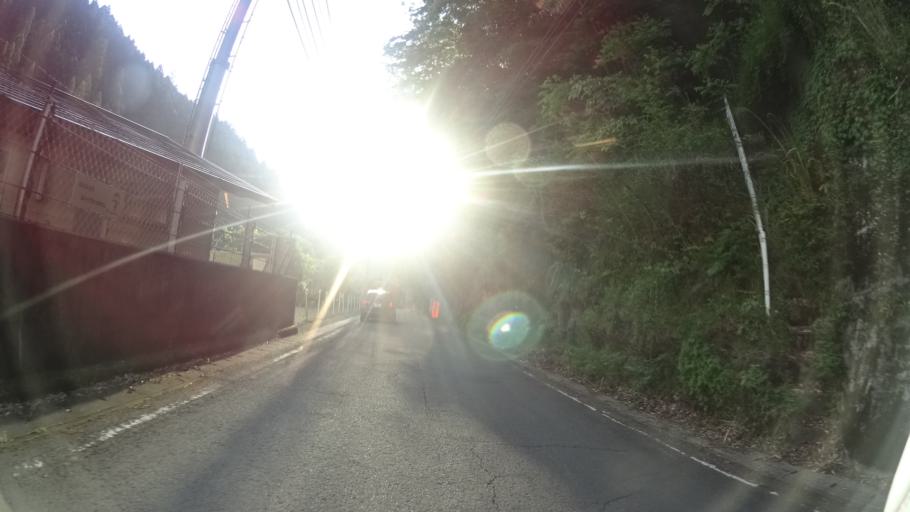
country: JP
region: Tokushima
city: Ikedacho
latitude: 33.9564
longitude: 133.8013
